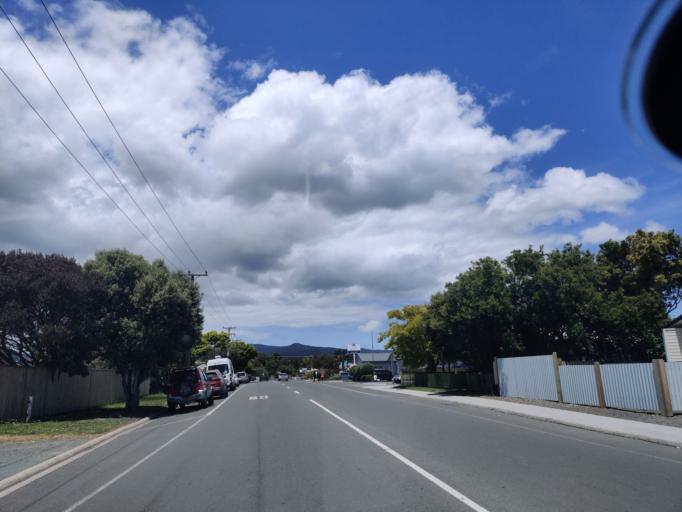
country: NZ
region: Northland
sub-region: Far North District
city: Kaitaia
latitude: -35.1093
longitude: 173.2587
